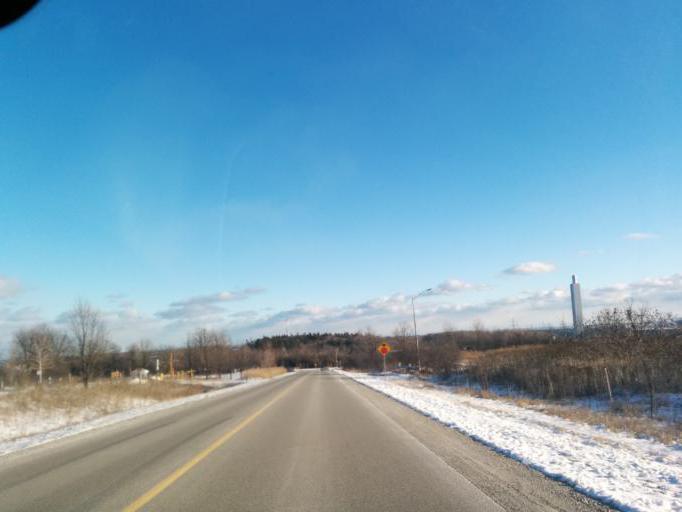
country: CA
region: Ontario
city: Oakville
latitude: 43.4957
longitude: -79.6674
